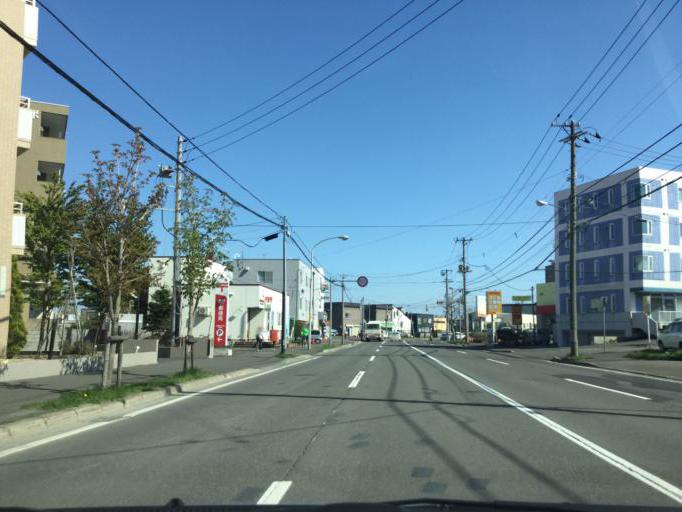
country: JP
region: Hokkaido
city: Sapporo
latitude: 43.0200
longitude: 141.4342
